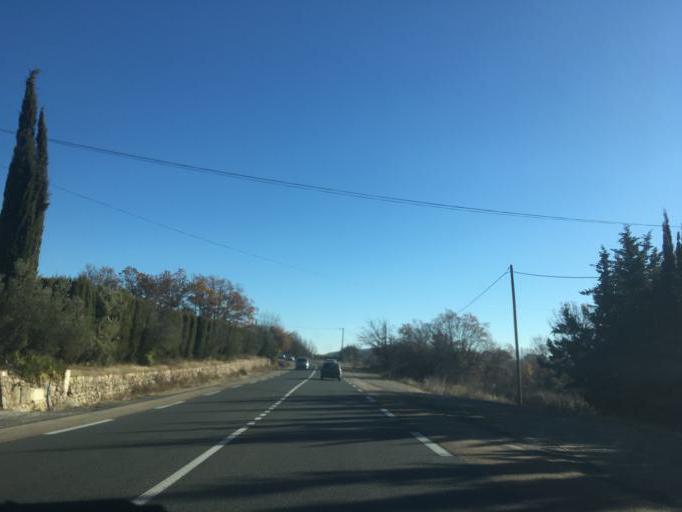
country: FR
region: Provence-Alpes-Cote d'Azur
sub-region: Departement du Var
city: Flayosc
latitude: 43.5294
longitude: 6.4188
